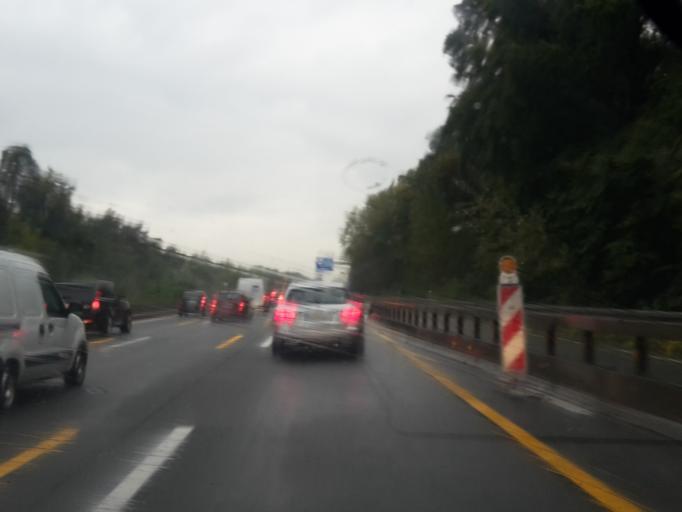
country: DE
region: Hesse
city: Lorsch
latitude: 49.6464
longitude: 8.5525
